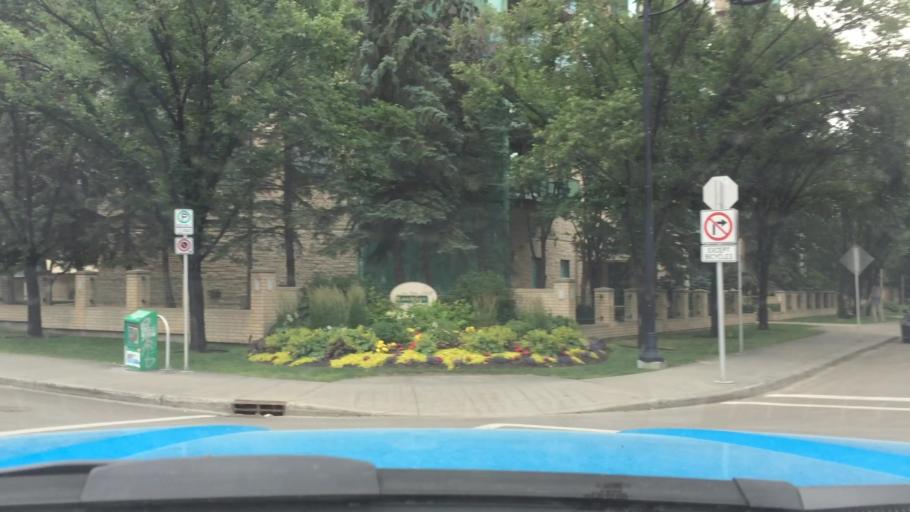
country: CA
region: Alberta
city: Calgary
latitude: 51.0517
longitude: -114.0784
